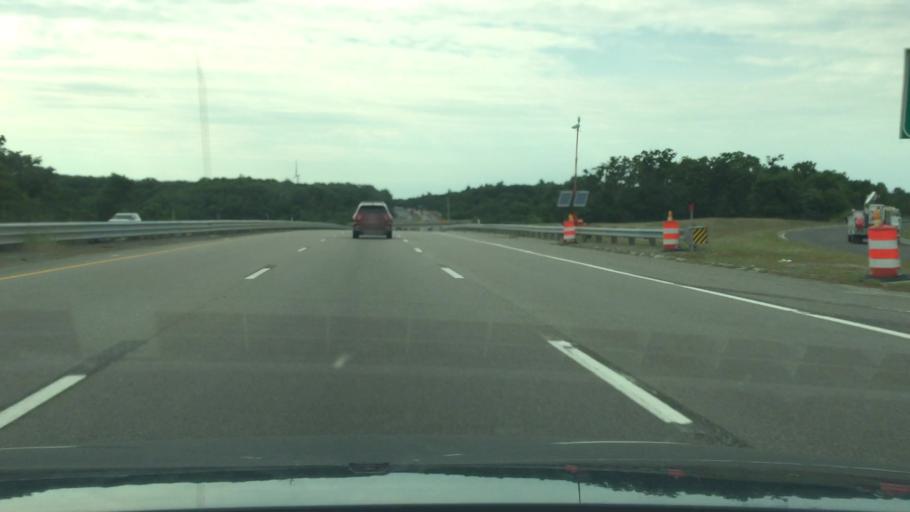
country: US
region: Massachusetts
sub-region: Plymouth County
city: North Plymouth
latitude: 41.9634
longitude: -70.6933
